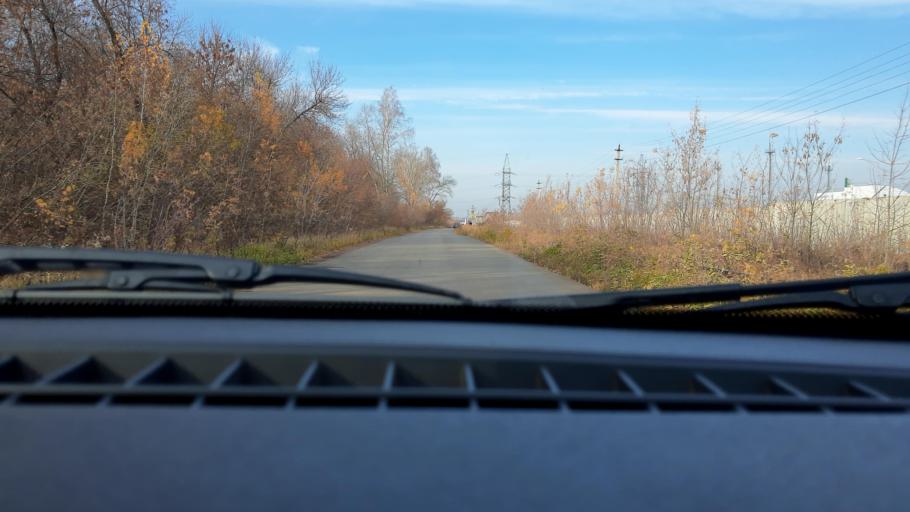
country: RU
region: Bashkortostan
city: Ufa
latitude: 54.5886
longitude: 55.9036
